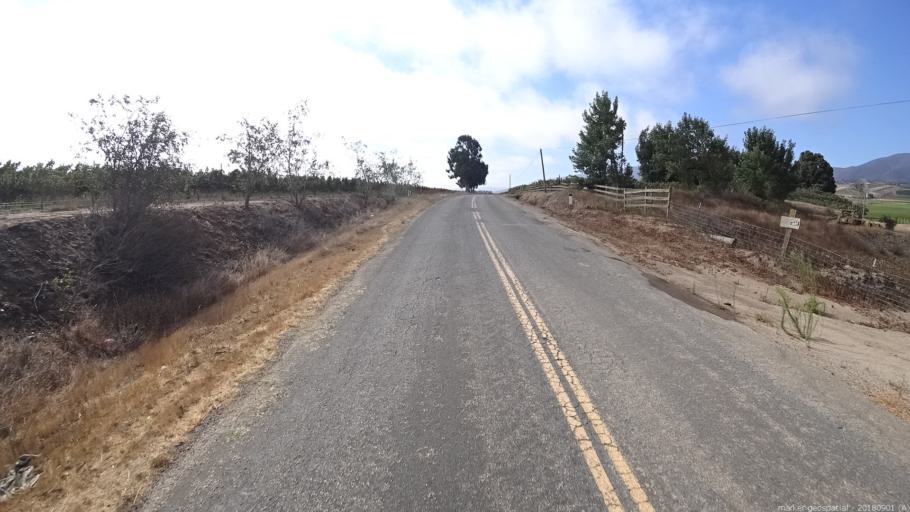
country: US
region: California
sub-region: Monterey County
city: Soledad
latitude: 36.3728
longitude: -121.3370
